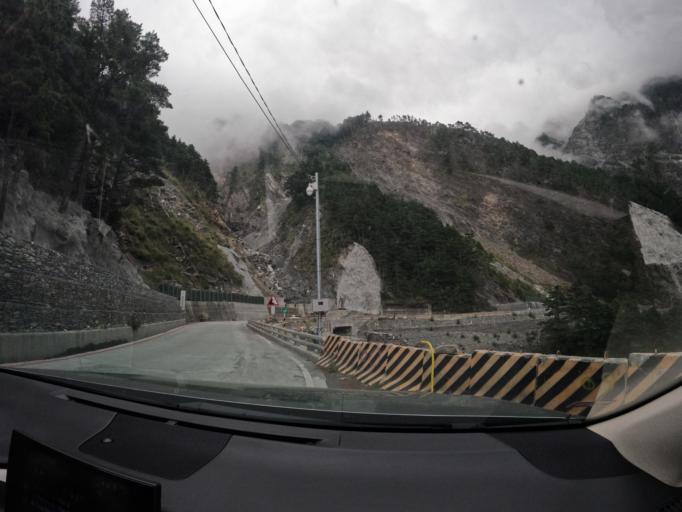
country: TW
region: Taiwan
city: Lugu
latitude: 23.2716
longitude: 120.9746
